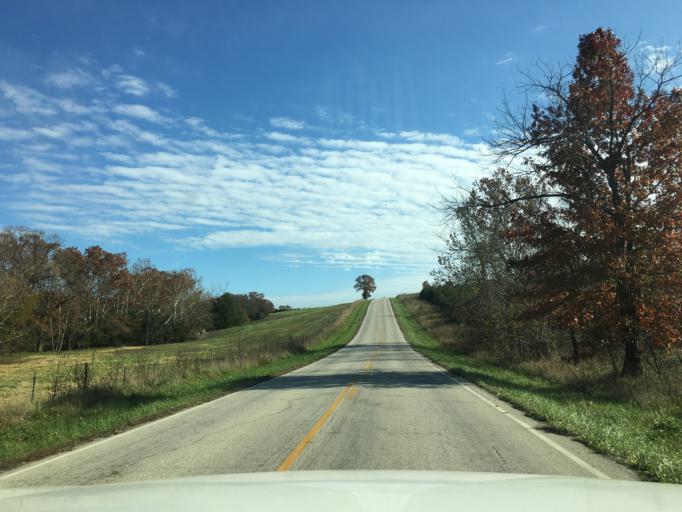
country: US
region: Missouri
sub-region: Maries County
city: Belle
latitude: 38.3379
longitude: -91.7827
